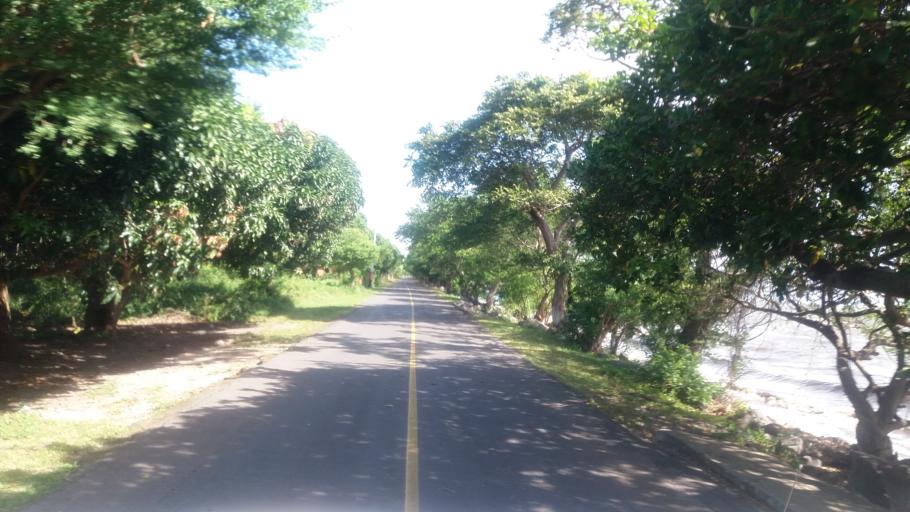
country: NI
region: Granada
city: Granada
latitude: 11.9771
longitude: -85.9418
